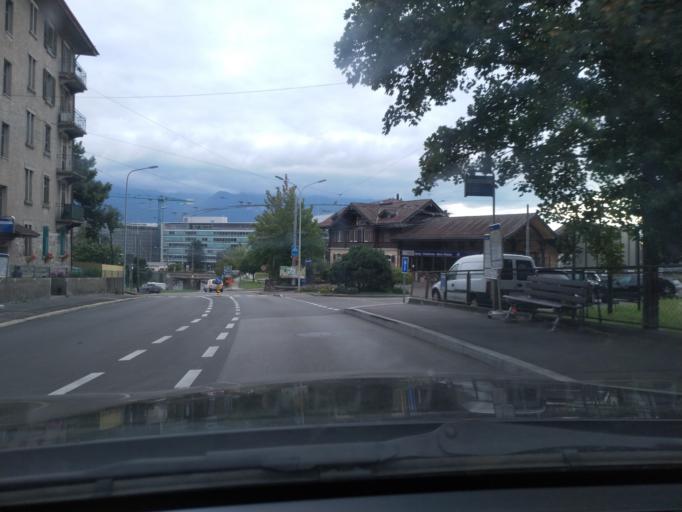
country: CH
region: Vaud
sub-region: Riviera-Pays-d'Enhaut District
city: Vevey
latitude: 46.4690
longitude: 6.8367
